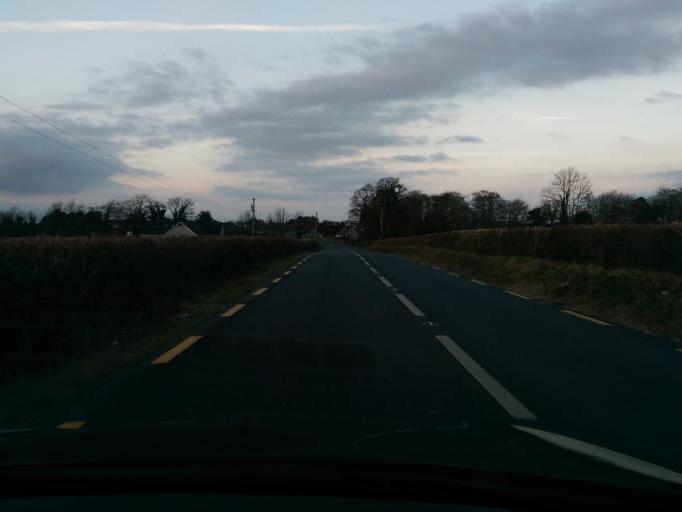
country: IE
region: Munster
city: Nenagh Bridge
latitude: 52.9759
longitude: -8.1324
